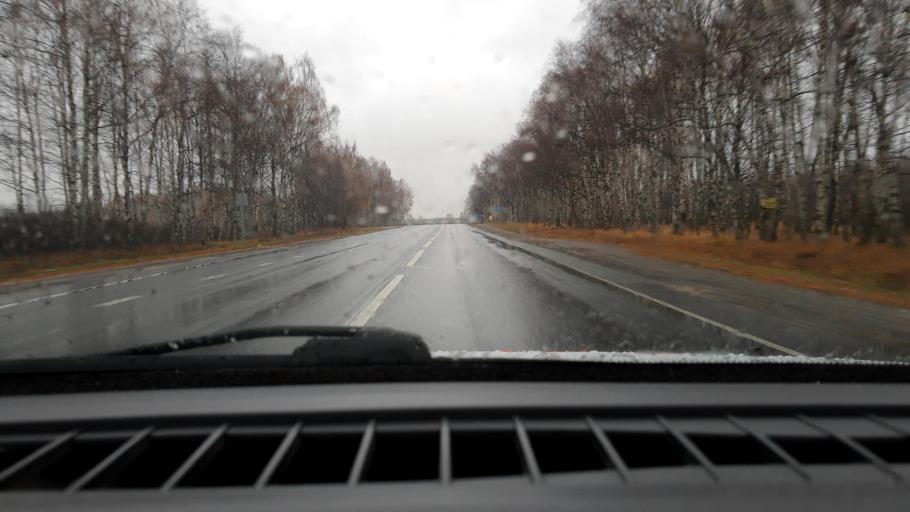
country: RU
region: Nizjnij Novgorod
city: Sitniki
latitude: 56.5211
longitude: 44.0258
